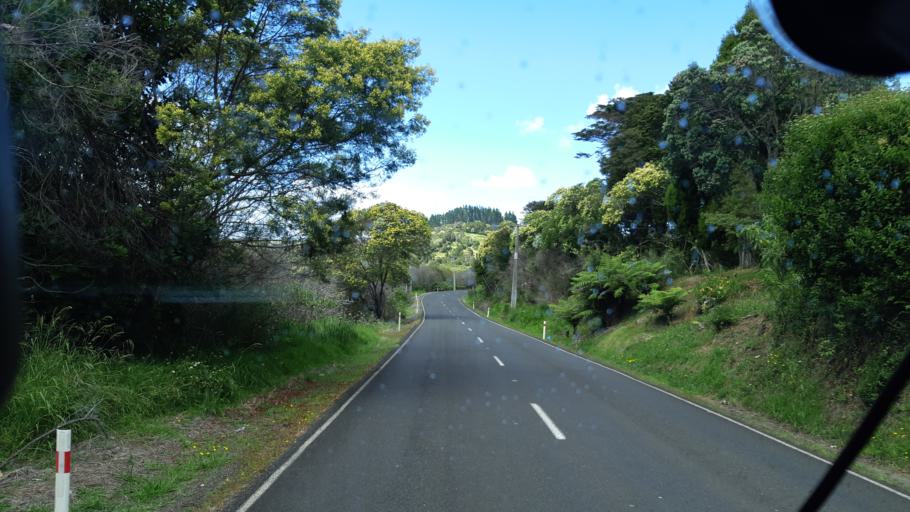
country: NZ
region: Northland
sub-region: Far North District
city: Taipa
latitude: -35.2698
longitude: 173.5230
